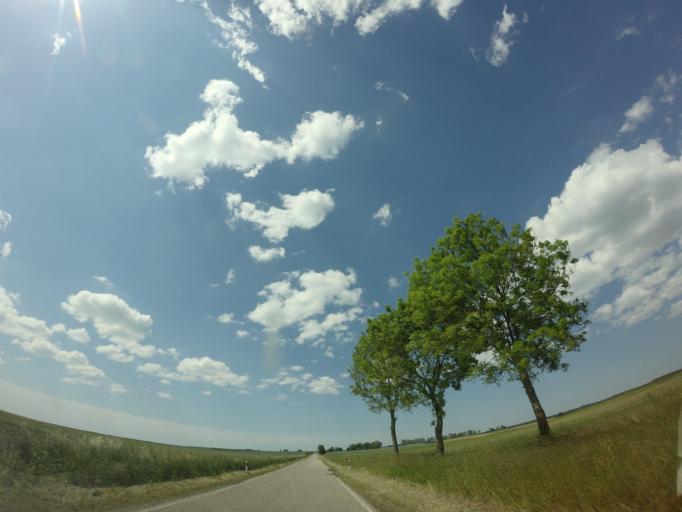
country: PL
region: West Pomeranian Voivodeship
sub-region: Powiat stargardzki
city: Dolice
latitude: 53.1685
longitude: 15.2231
